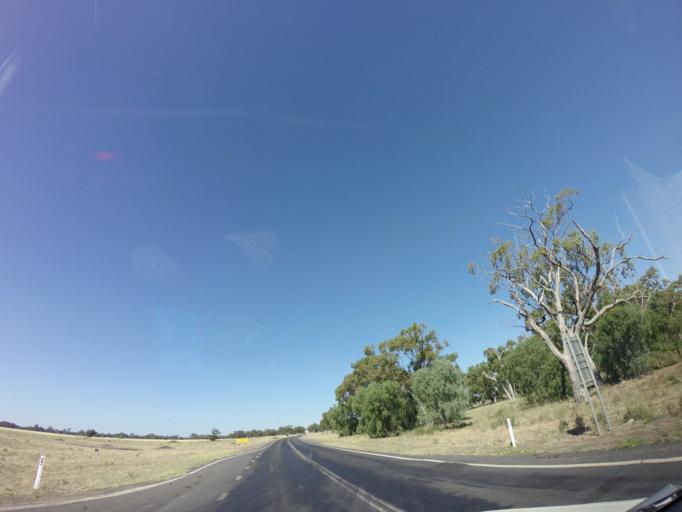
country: AU
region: New South Wales
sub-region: Bogan
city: Nyngan
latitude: -31.6635
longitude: 147.8620
